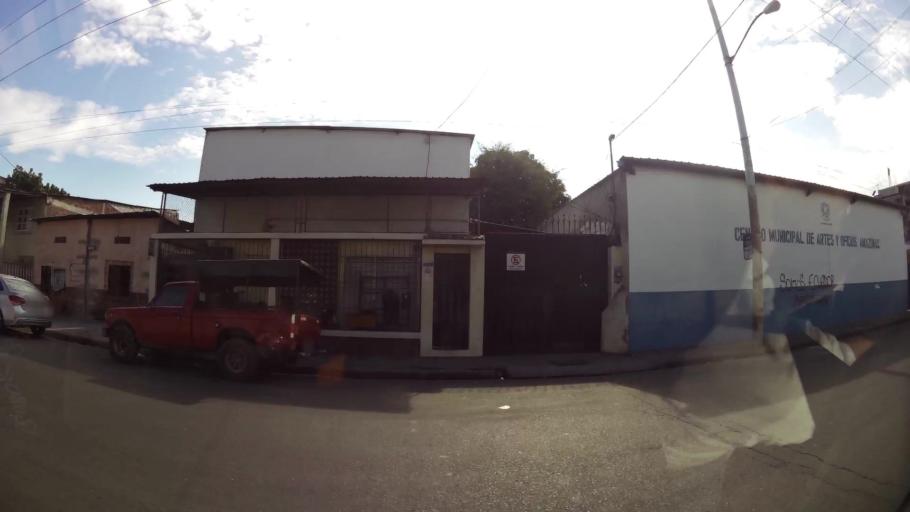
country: EC
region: Guayas
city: Guayaquil
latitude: -2.1963
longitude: -79.9249
